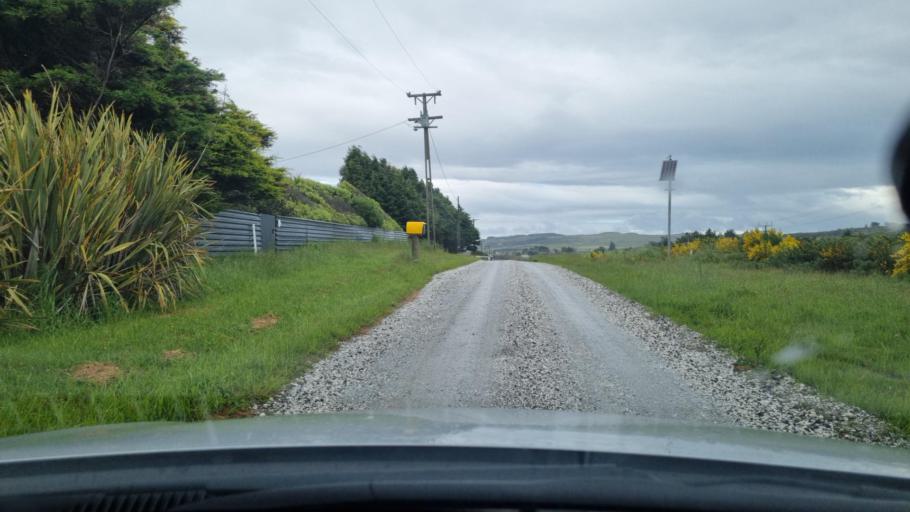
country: NZ
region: Southland
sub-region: Invercargill City
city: Bluff
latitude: -46.5442
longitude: 168.3018
